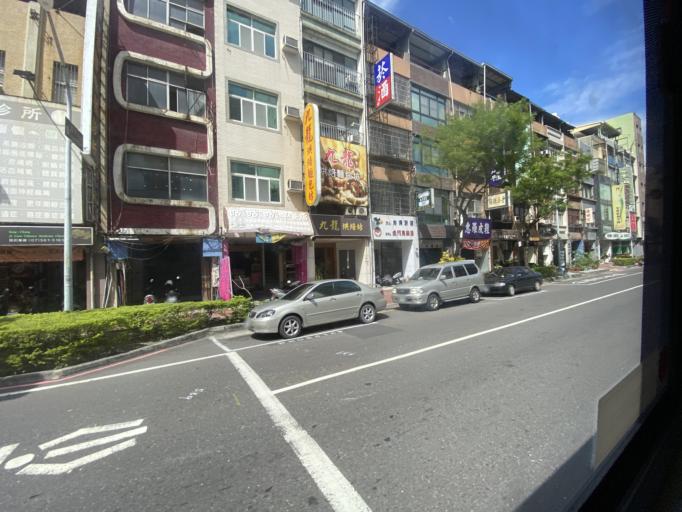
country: TW
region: Kaohsiung
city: Kaohsiung
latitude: 22.6239
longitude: 120.2830
